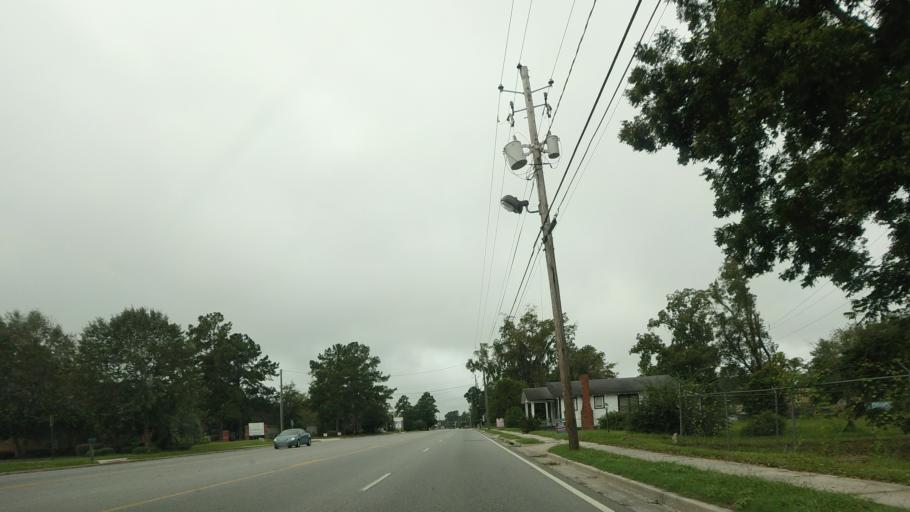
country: US
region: Georgia
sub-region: Lowndes County
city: Valdosta
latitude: 30.8234
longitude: -83.2993
